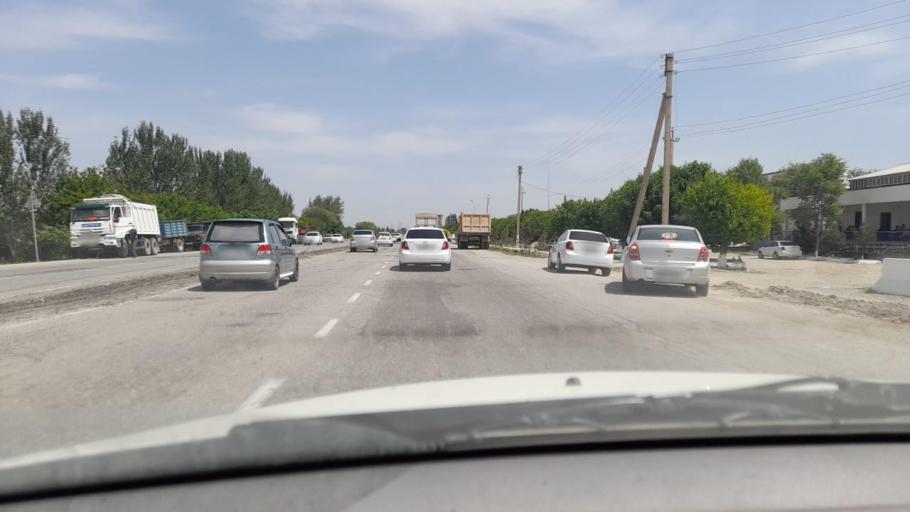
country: UZ
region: Navoiy
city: Beshrabot
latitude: 40.1417
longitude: 65.2924
